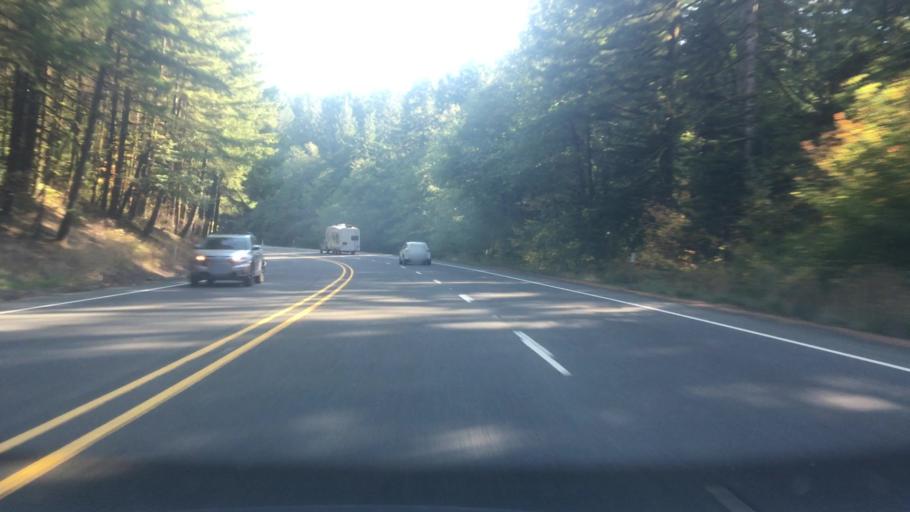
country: US
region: Oregon
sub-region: Polk County
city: Grand Ronde
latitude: 45.0615
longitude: -123.7018
